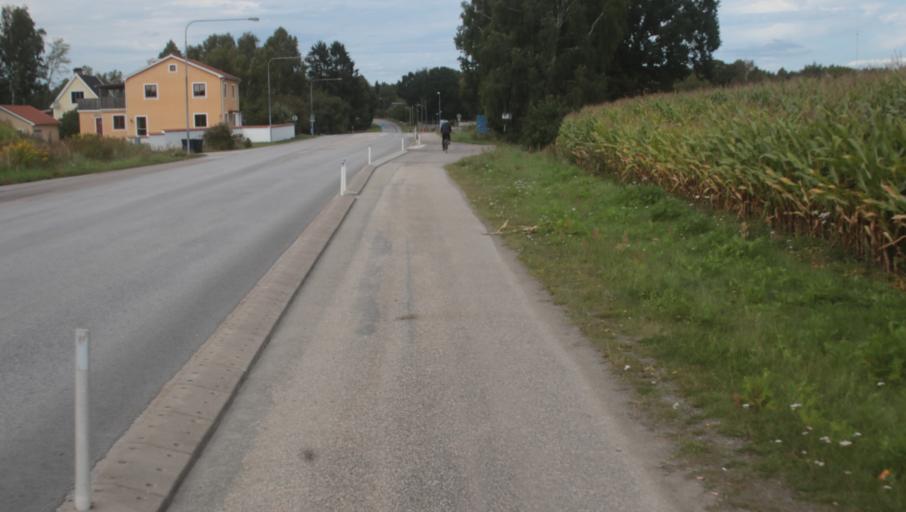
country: SE
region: Blekinge
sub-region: Karlshamns Kommun
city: Karlshamn
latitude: 56.2123
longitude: 14.8345
